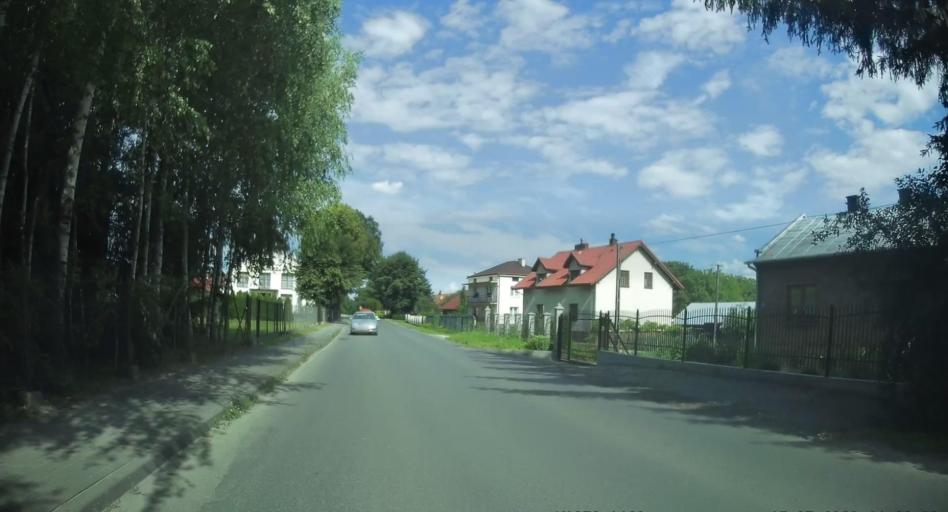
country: PL
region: Subcarpathian Voivodeship
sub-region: Powiat przemyski
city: Zurawica
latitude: 49.8023
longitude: 22.7986
